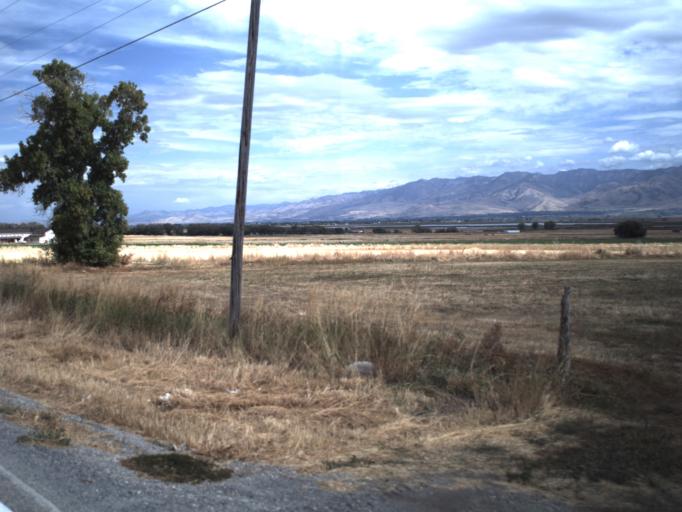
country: US
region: Utah
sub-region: Cache County
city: Mendon
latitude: 41.7331
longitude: -111.9792
